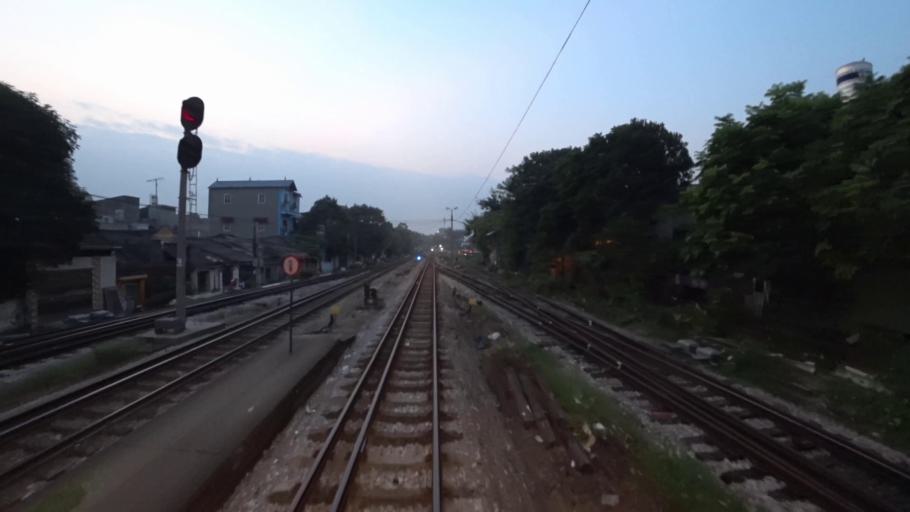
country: VN
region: Ha Noi
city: Soc Son
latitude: 21.2442
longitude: 105.8615
